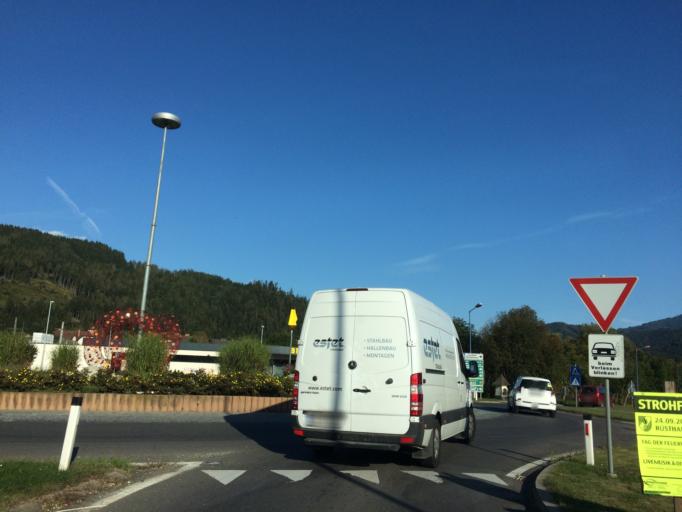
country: AT
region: Styria
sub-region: Politischer Bezirk Leoben
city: Sankt Michael in Obersteiermark
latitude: 47.3391
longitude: 15.0123
